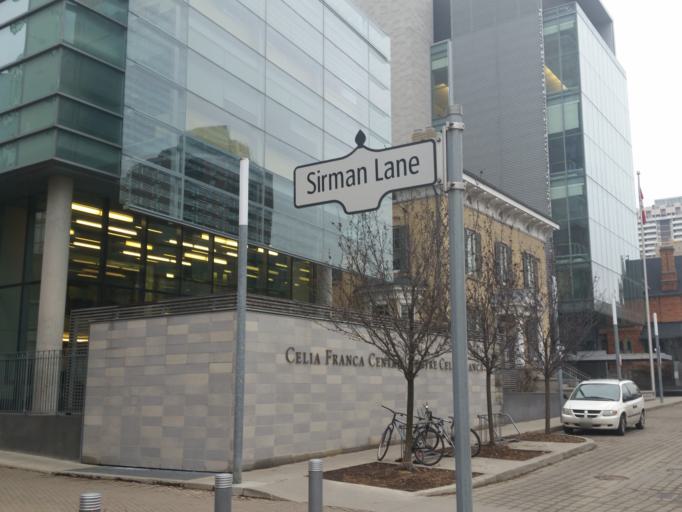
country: CA
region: Ontario
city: Toronto
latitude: 43.6635
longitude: -79.3773
